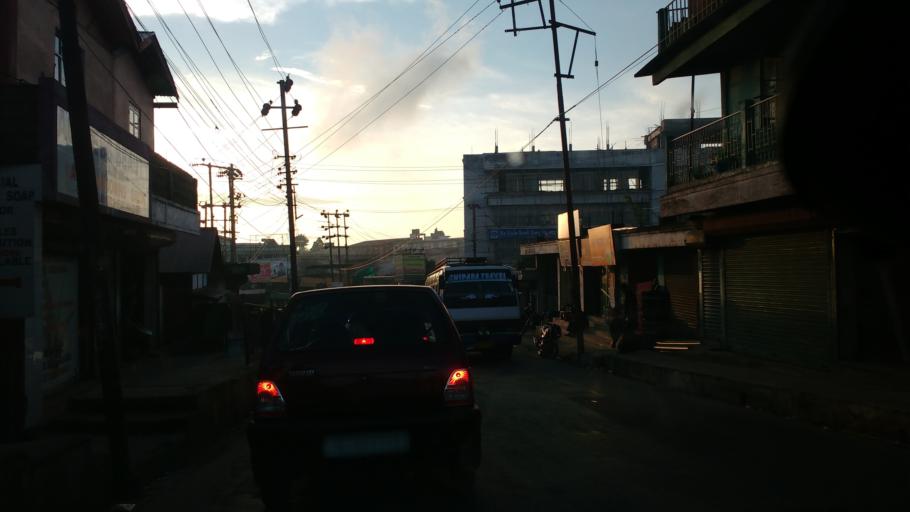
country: IN
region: Meghalaya
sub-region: East Khasi Hills
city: Shillong
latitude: 25.5641
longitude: 91.9034
